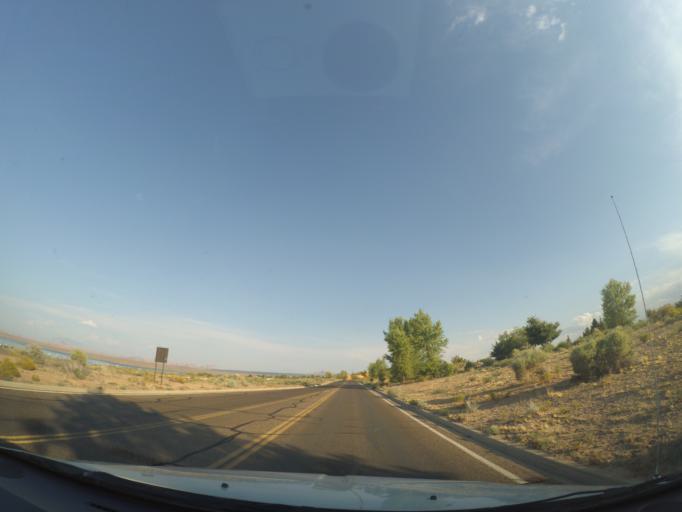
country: US
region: Arizona
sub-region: Coconino County
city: Page
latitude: 37.0014
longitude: -111.5010
